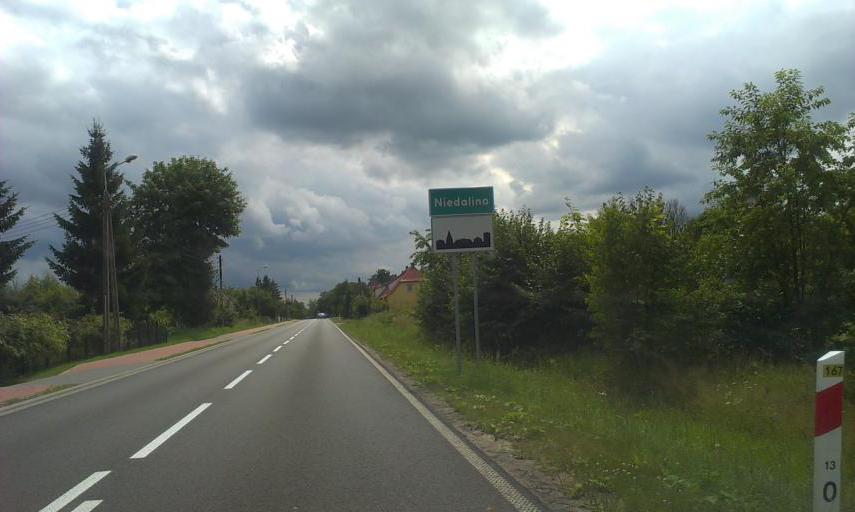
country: PL
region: West Pomeranian Voivodeship
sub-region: Koszalin
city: Koszalin
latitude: 54.0722
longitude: 16.1627
